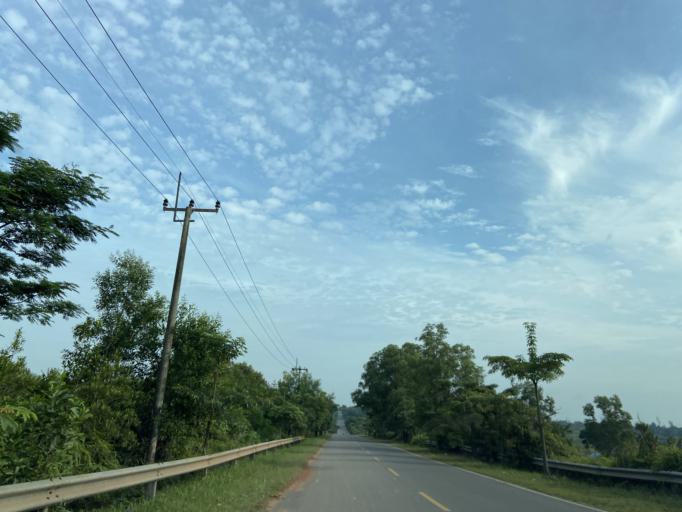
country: ID
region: Riau Islands
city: Tanjungpinang
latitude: 0.9189
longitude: 104.1186
